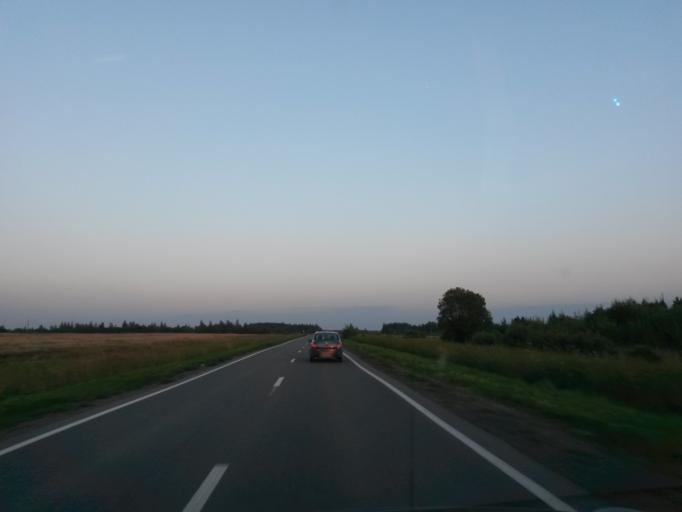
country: RU
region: Jaroslavl
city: Konstantinovskiy
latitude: 57.8730
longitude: 39.5911
